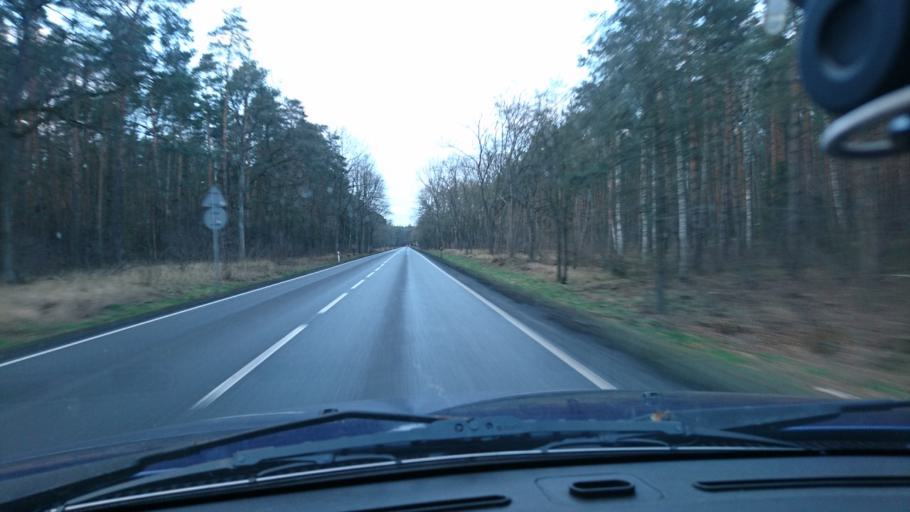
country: PL
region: Greater Poland Voivodeship
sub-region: Powiat kepinski
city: Kepno
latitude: 51.3331
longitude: 17.9572
